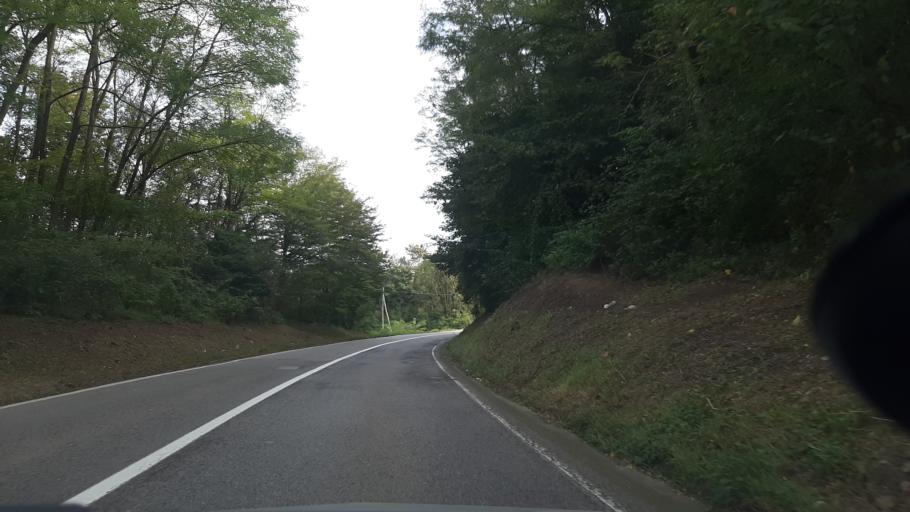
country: BA
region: Republika Srpska
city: Maglajani
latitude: 44.8797
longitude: 17.3721
